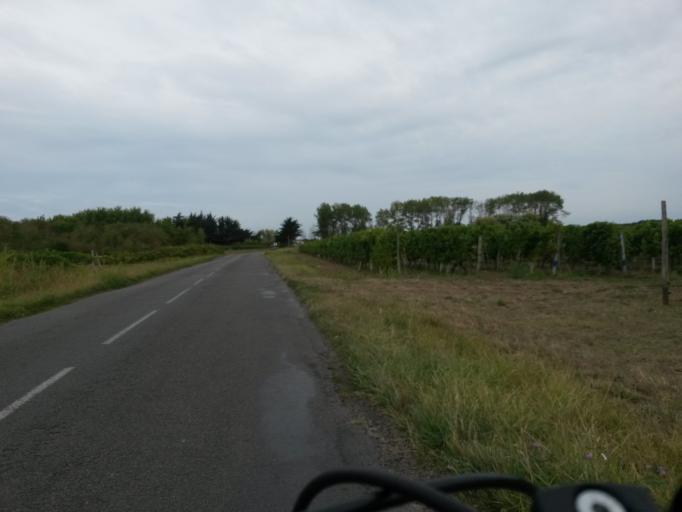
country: FR
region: Poitou-Charentes
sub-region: Departement de la Charente-Maritime
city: Dolus-d'Oleron
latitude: 45.9314
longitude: -1.3312
